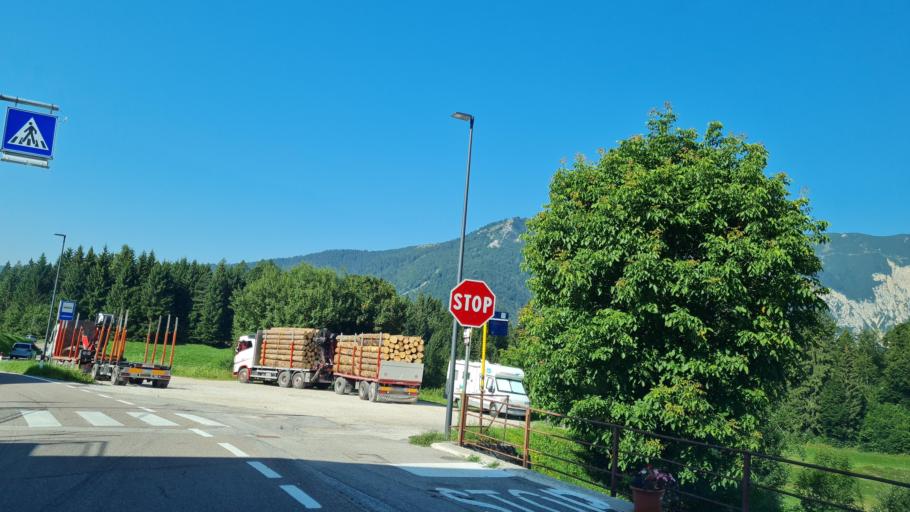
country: IT
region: Trentino-Alto Adige
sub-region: Provincia di Trento
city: Centa San Nicolo
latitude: 45.9458
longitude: 11.2389
